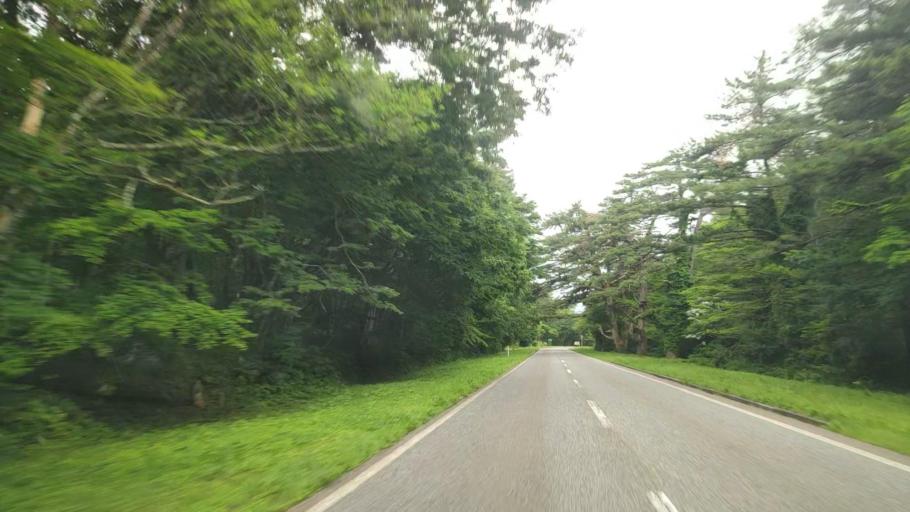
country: JP
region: Tottori
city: Yonago
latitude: 35.3994
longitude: 133.5021
